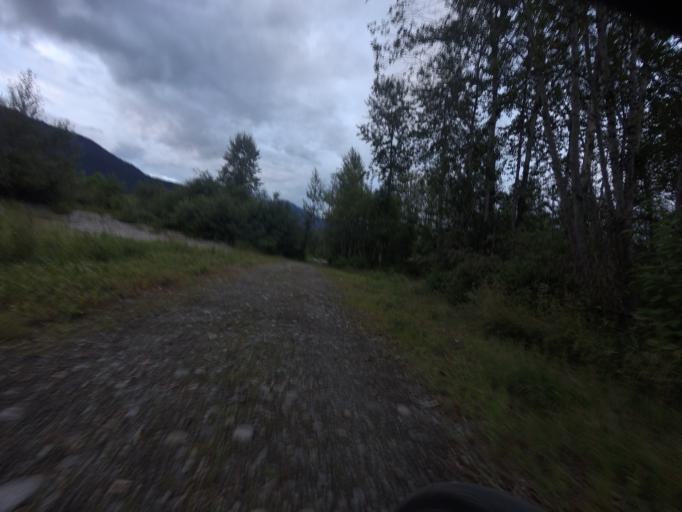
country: CA
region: British Columbia
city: Pemberton
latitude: 50.3148
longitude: -122.8047
